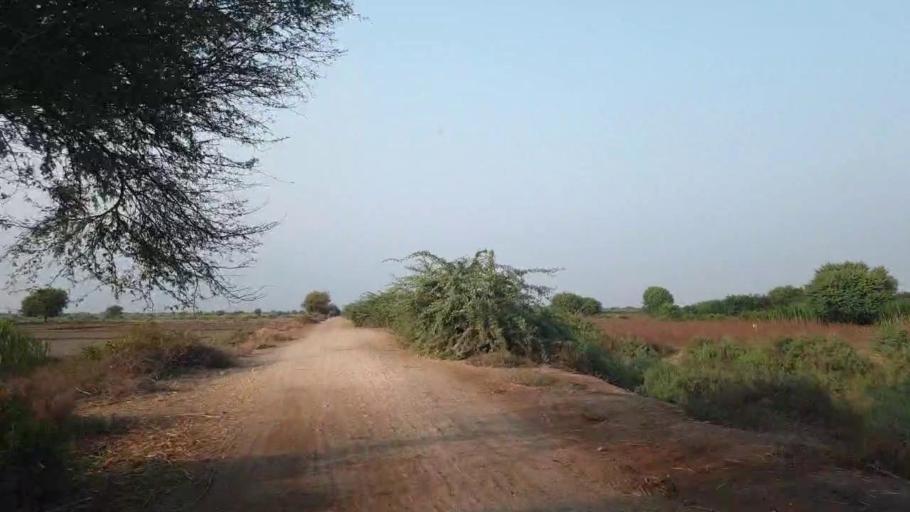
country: PK
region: Sindh
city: Tando Ghulam Ali
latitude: 25.0535
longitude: 68.9605
